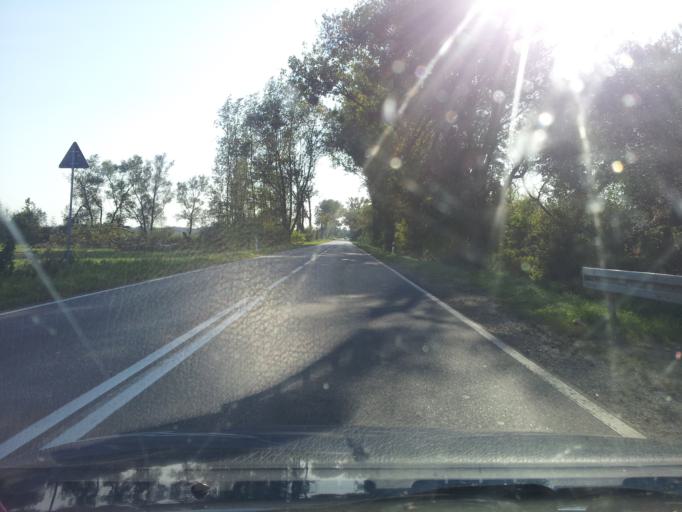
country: PL
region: Masovian Voivodeship
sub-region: Powiat nowodworski
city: Nowy Dwor Mazowiecki
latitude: 52.4080
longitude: 20.6928
